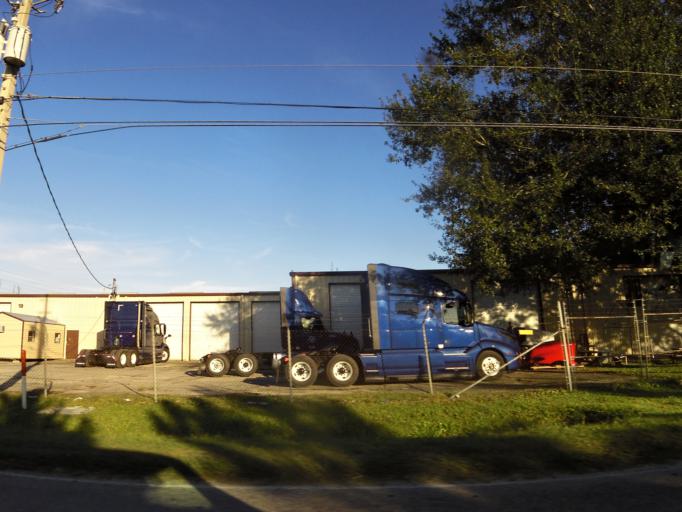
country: US
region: Florida
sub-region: Duval County
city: Jacksonville
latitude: 30.3423
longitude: -81.7646
